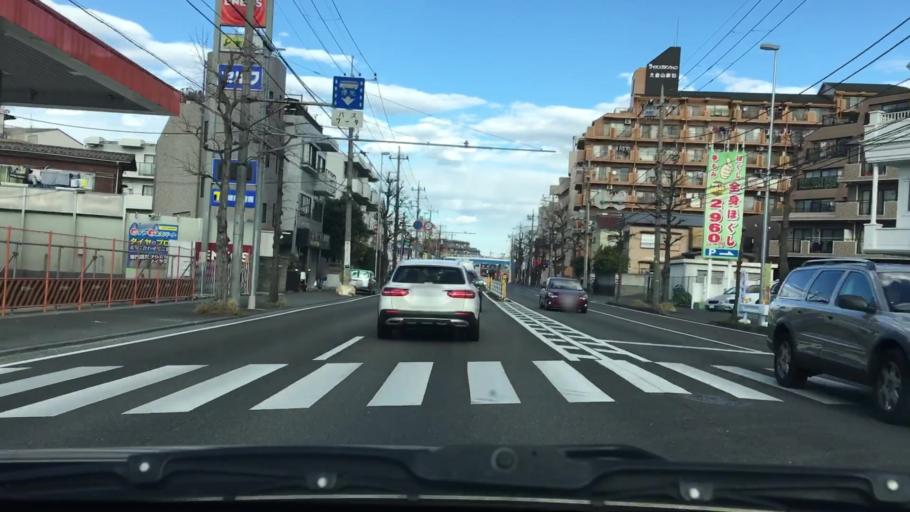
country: JP
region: Kanagawa
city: Yokohama
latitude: 35.5220
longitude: 139.6382
